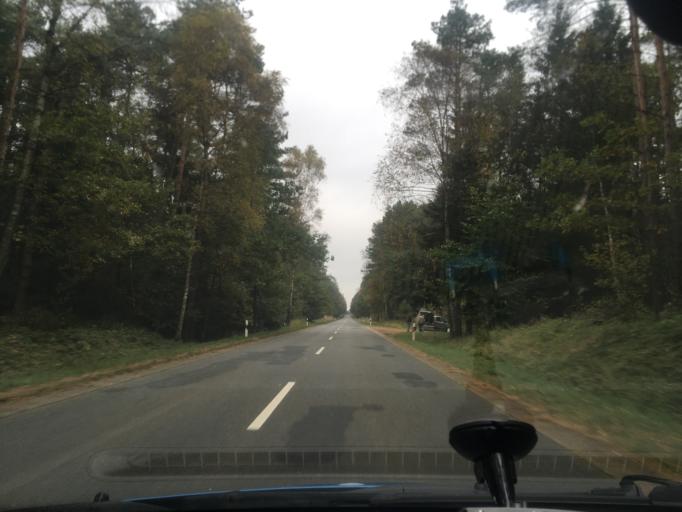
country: DE
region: Lower Saxony
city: Bispingen
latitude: 53.0807
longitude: 10.0366
